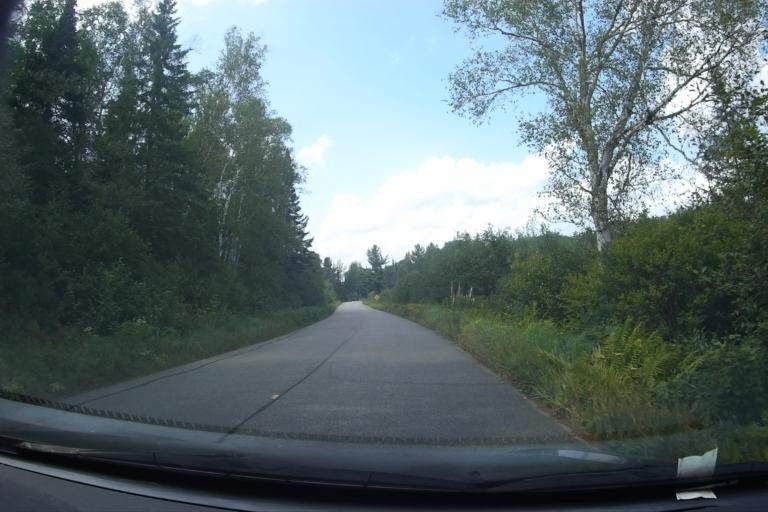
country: CA
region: Ontario
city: Bancroft
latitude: 45.5974
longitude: -78.3284
